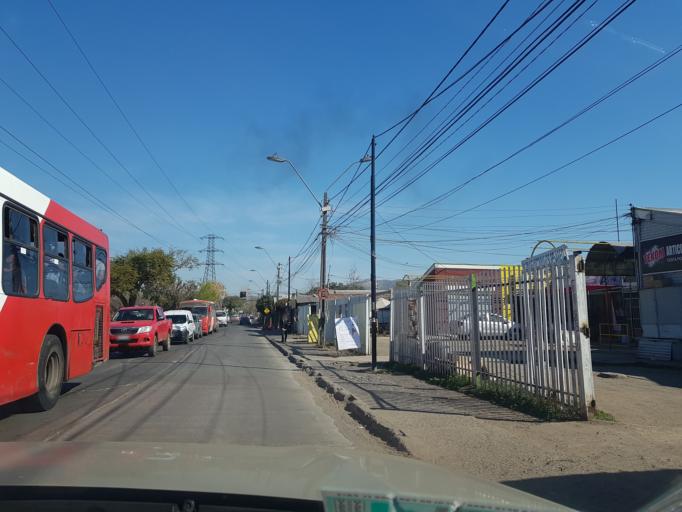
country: CL
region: Santiago Metropolitan
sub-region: Provincia de Santiago
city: Lo Prado
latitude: -33.3670
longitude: -70.7199
